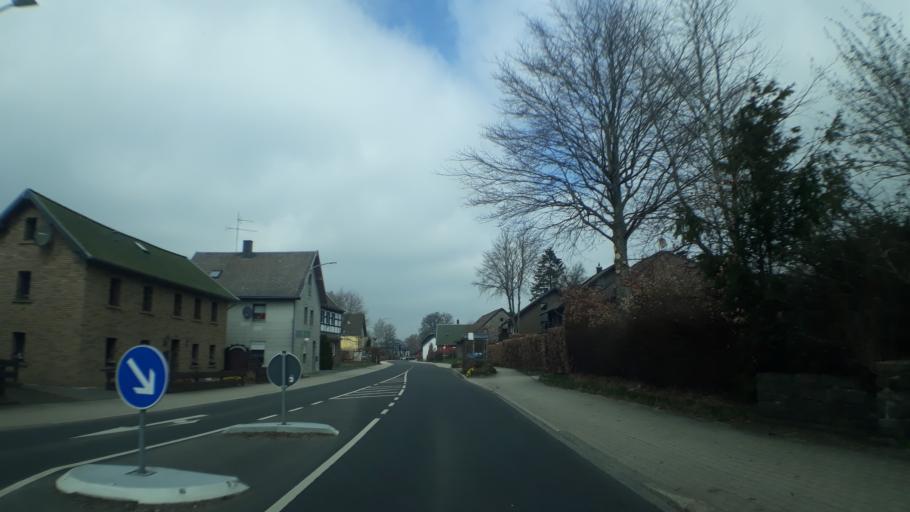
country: DE
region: North Rhine-Westphalia
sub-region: Regierungsbezirk Koln
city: Monschau
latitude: 50.5165
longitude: 6.2188
